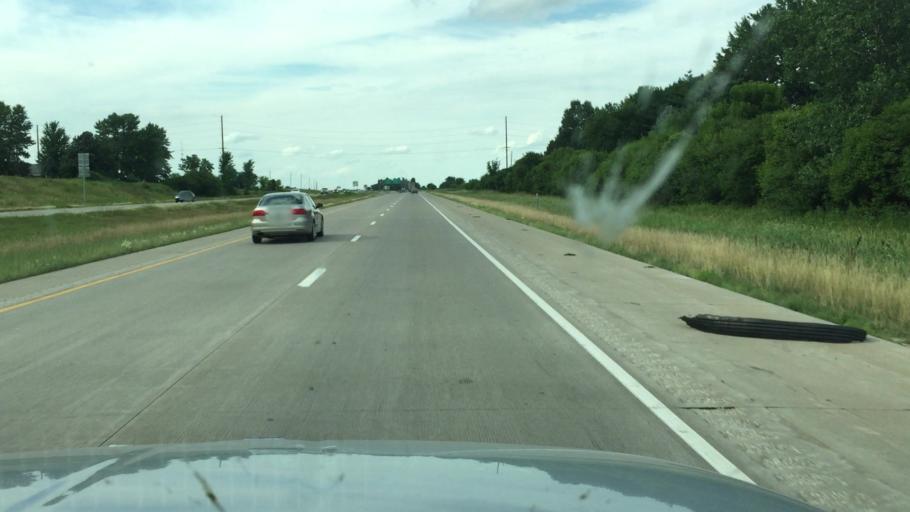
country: US
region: Iowa
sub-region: Scott County
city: Walcott
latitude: 41.5794
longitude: -90.6767
